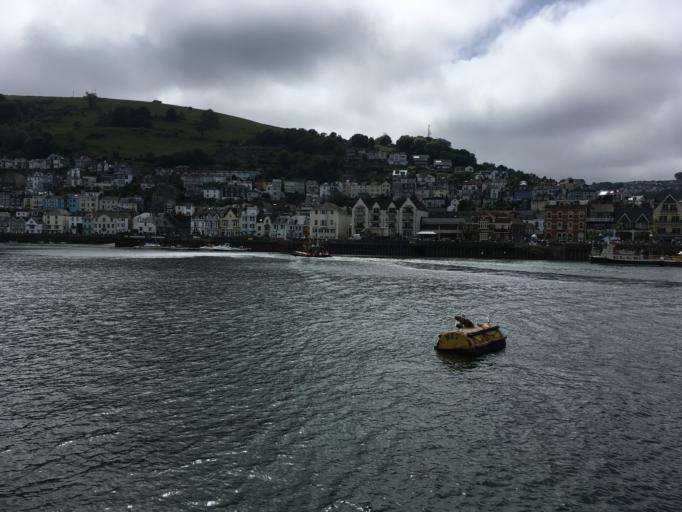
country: GB
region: England
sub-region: Devon
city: Dartmouth
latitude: 50.3506
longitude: -3.5749
